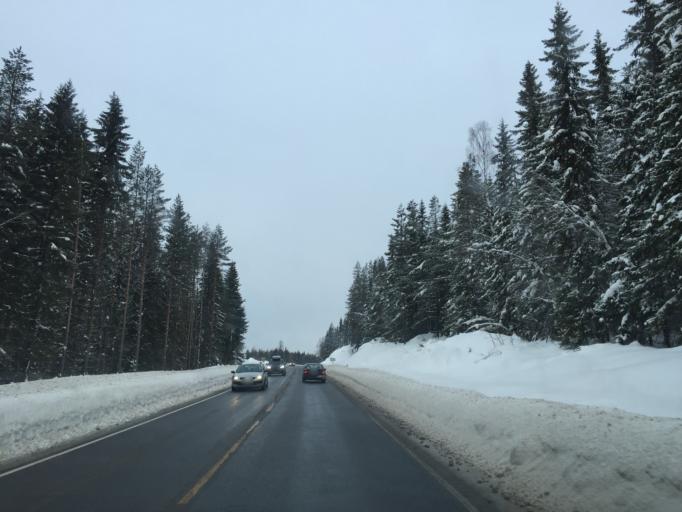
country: NO
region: Hedmark
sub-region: Trysil
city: Innbygda
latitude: 61.0930
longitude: 12.0022
